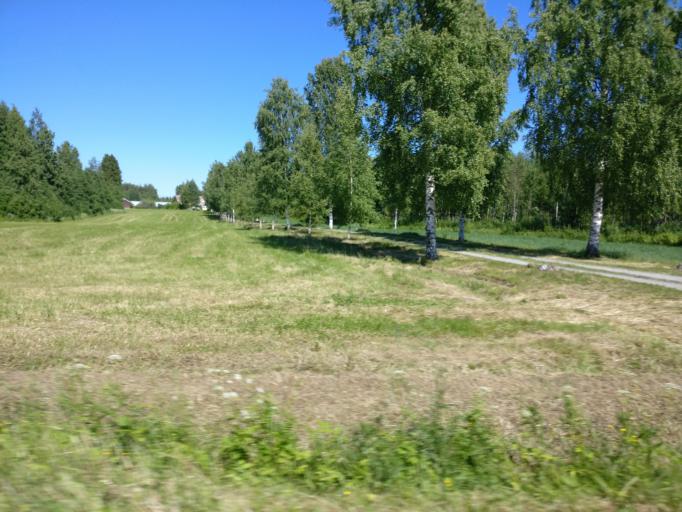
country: FI
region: Southern Savonia
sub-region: Savonlinna
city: Rantasalmi
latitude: 62.0803
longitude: 28.2998
